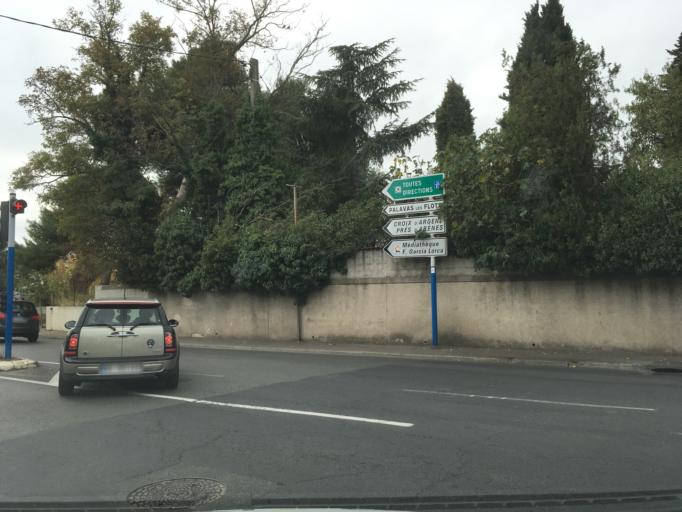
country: FR
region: Languedoc-Roussillon
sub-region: Departement de l'Herault
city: Montpellier
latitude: 43.5930
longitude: 3.8898
